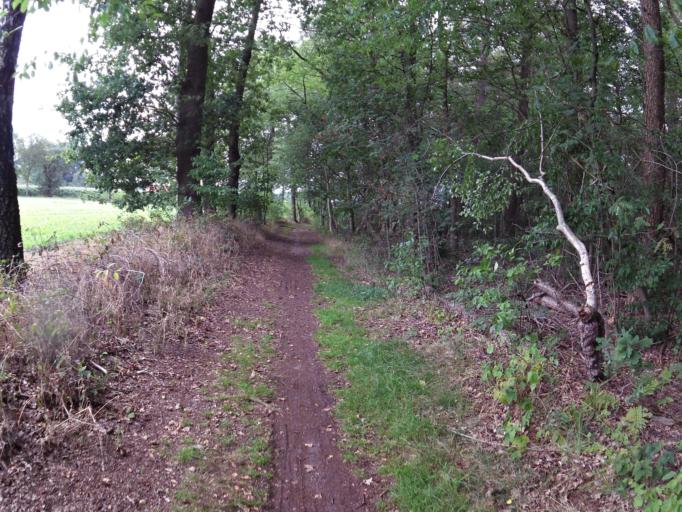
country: DE
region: North Rhine-Westphalia
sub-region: Regierungsbezirk Munster
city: Gronau
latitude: 52.1774
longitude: 6.9851
